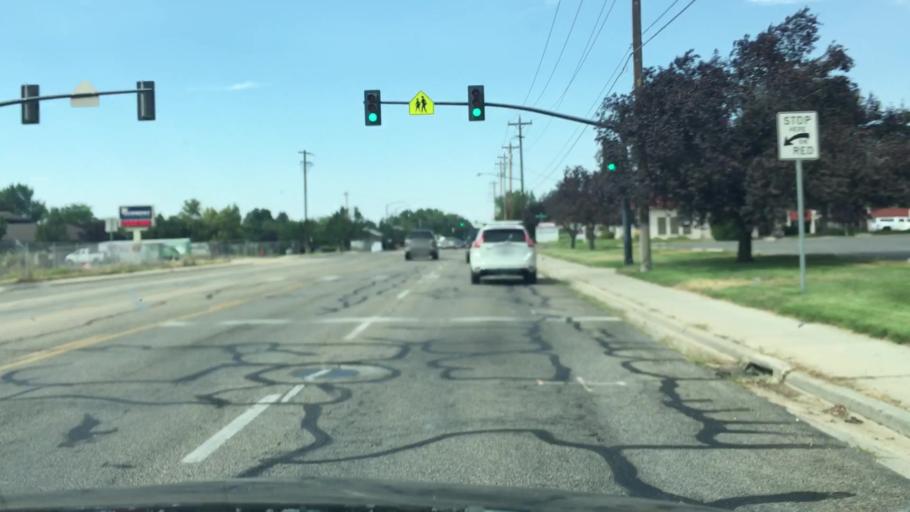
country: US
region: Idaho
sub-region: Ada County
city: Garden City
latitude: 43.6247
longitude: -116.2742
